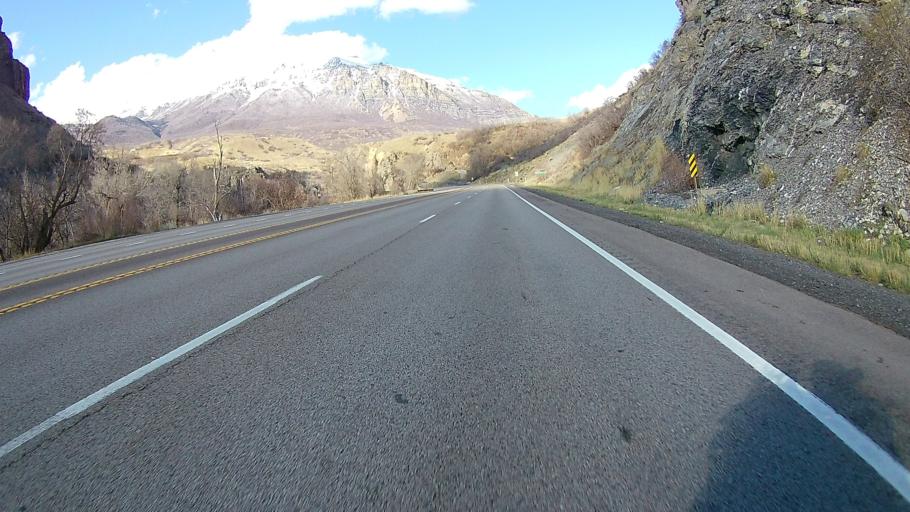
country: US
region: Utah
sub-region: Utah County
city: Orem
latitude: 40.3167
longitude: -111.6518
